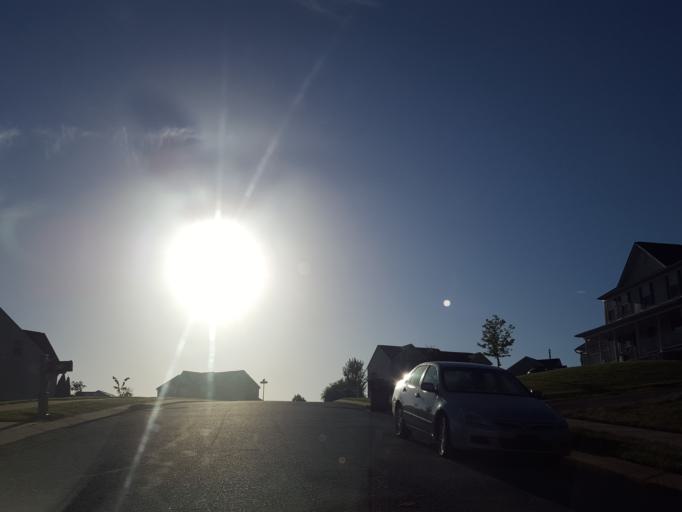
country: US
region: Pennsylvania
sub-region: York County
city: Windsor
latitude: 39.9470
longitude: -76.6091
